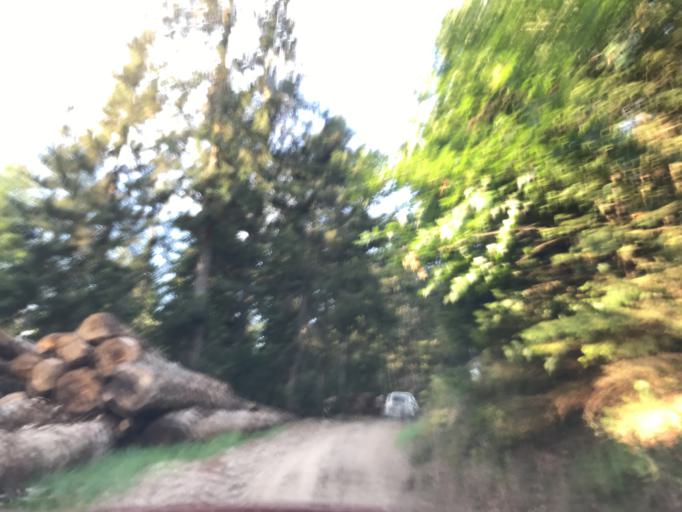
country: FR
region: Rhone-Alpes
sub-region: Departement de la Loire
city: Noiretable
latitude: 45.7610
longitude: 3.7603
